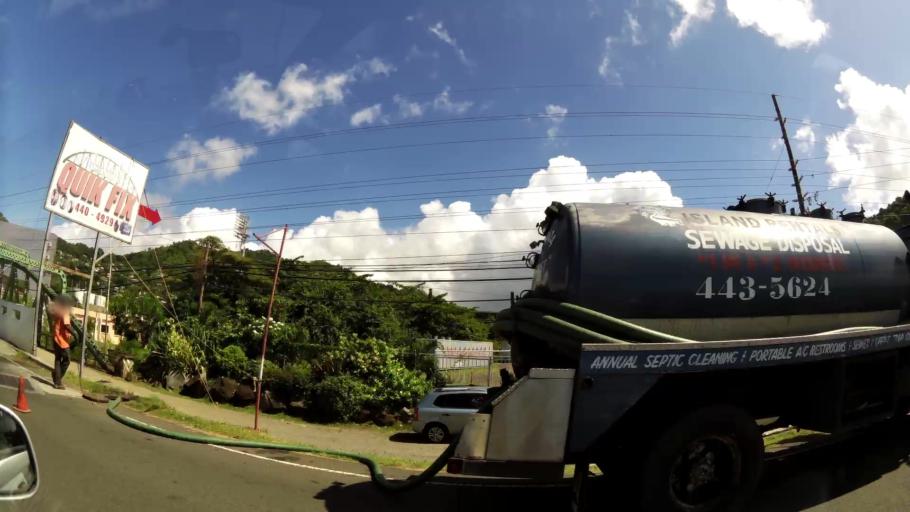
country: GD
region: Saint George
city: Saint George's
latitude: 12.0584
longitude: -61.7543
